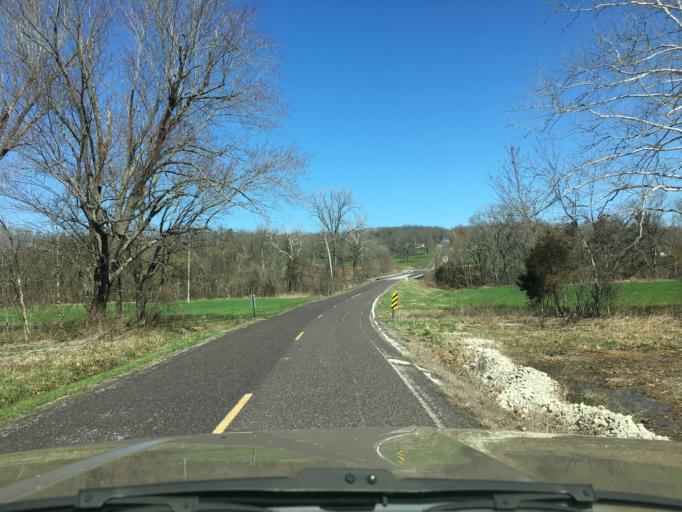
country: US
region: Missouri
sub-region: Franklin County
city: Gerald
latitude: 38.5268
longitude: -91.3309
